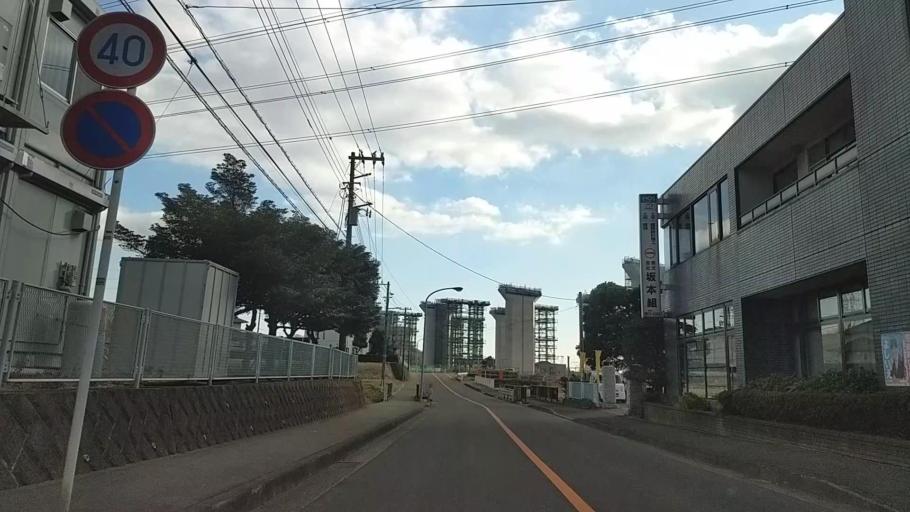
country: JP
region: Kanagawa
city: Isehara
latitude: 35.4169
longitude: 139.3000
